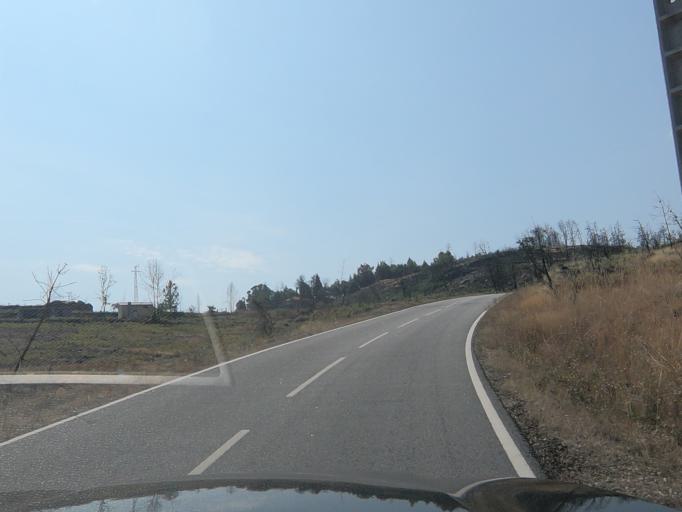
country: PT
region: Vila Real
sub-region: Sabrosa
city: Sabrosa
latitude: 41.3396
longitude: -7.5945
